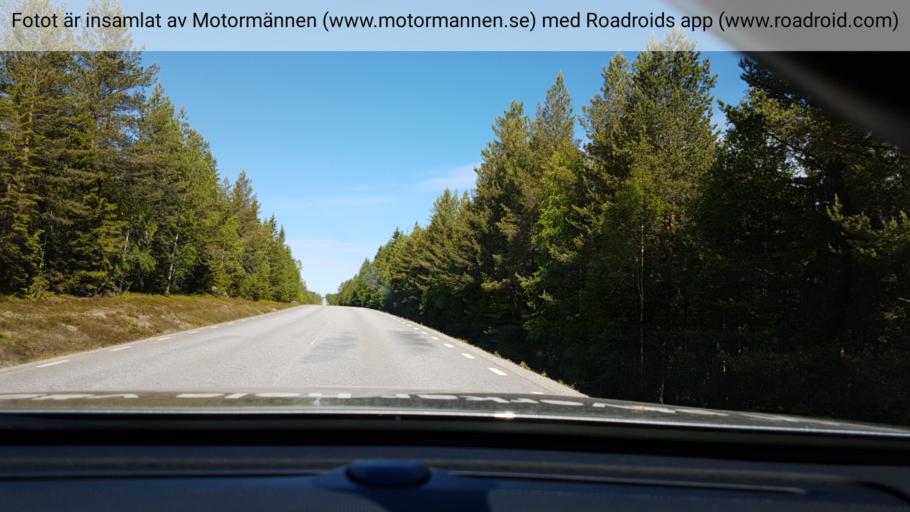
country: SE
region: Vaesterbotten
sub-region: Bjurholms Kommun
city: Bjurholm
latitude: 63.9405
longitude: 18.9288
